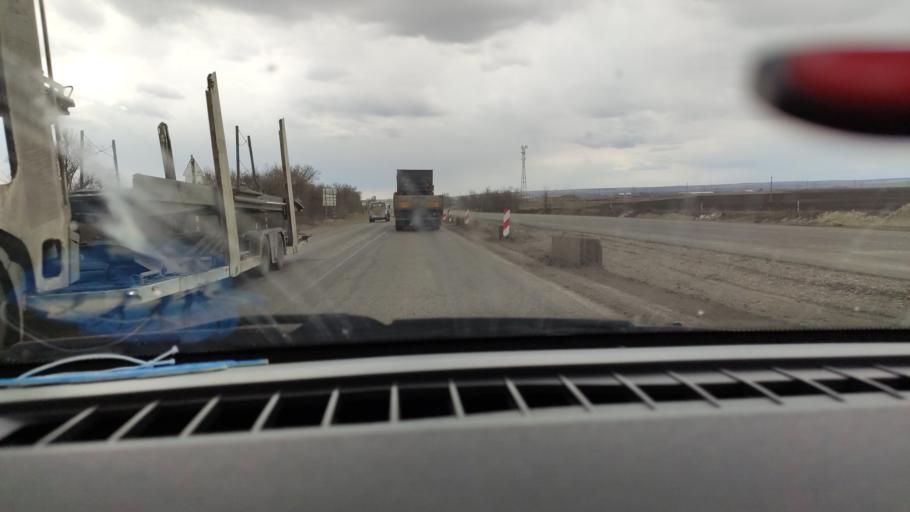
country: RU
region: Saratov
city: Sinodskoye
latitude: 51.9999
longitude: 46.6774
